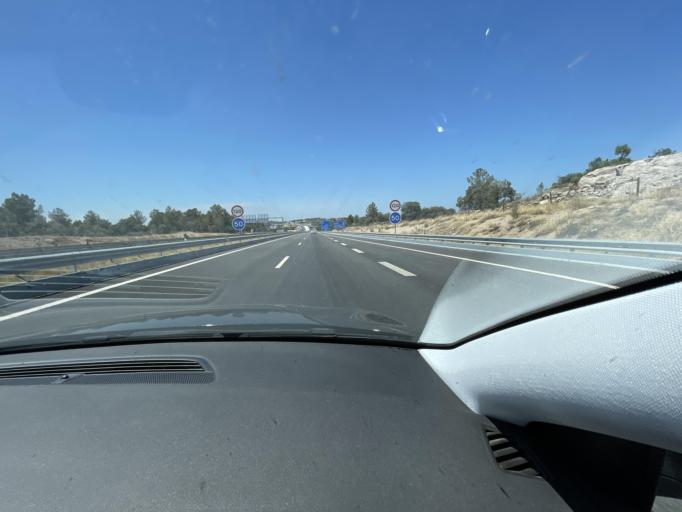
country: ES
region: Castille and Leon
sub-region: Provincia de Salamanca
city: Fuentes de Onoro
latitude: 40.6149
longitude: -6.8235
